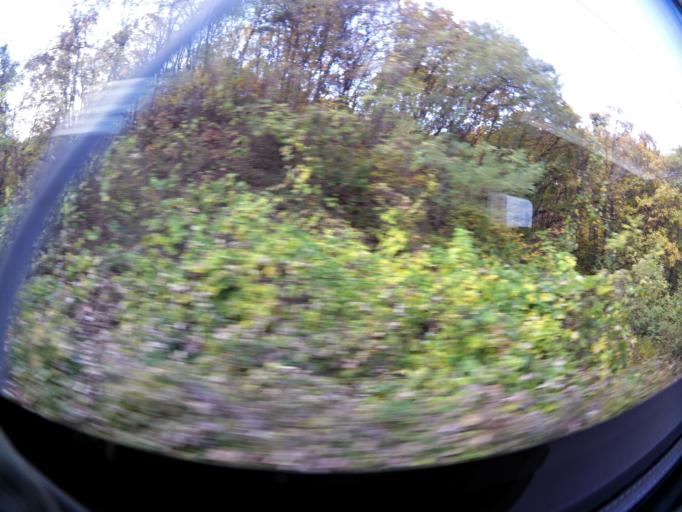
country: KR
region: Gyeongsangbuk-do
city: Gimcheon
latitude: 36.1731
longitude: 128.0070
